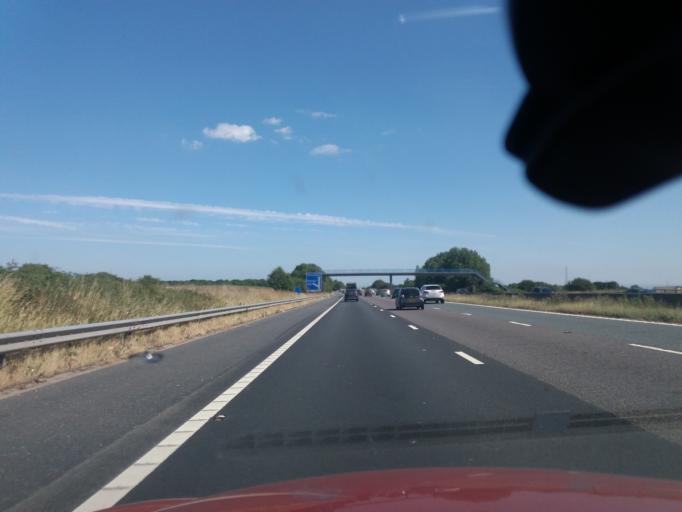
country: GB
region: England
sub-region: Borough of Wigan
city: Tyldesley
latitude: 53.5469
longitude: -2.4589
